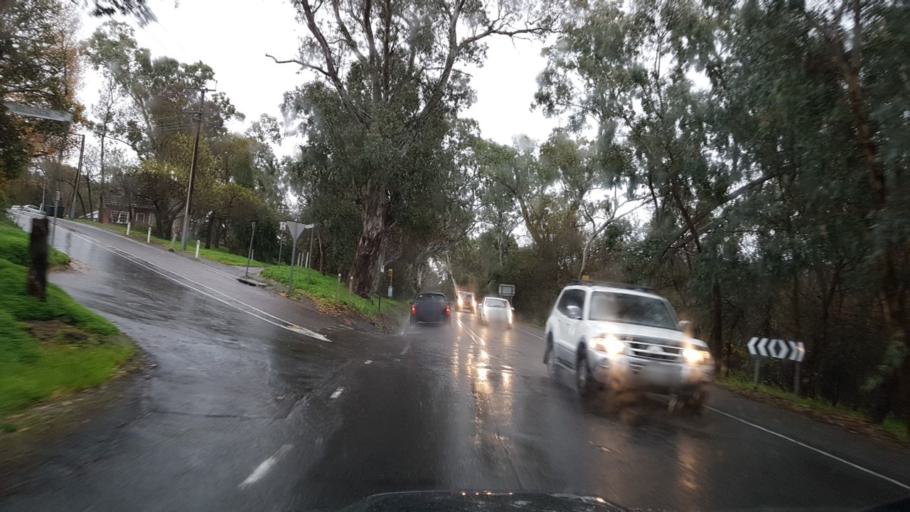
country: AU
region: South Australia
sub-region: Mitcham
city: Blackwood
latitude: -35.0284
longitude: 138.6251
